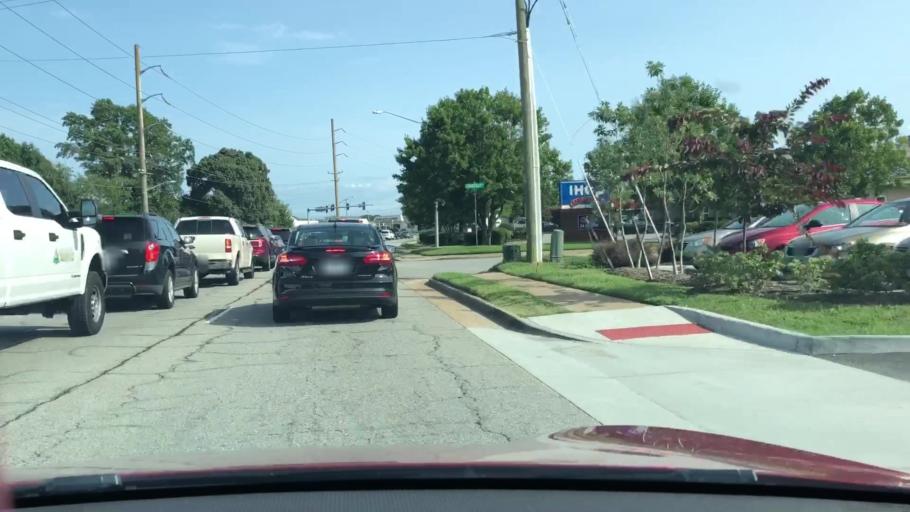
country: US
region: Virginia
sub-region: City of Virginia Beach
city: Virginia Beach
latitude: 36.8544
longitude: -76.0240
